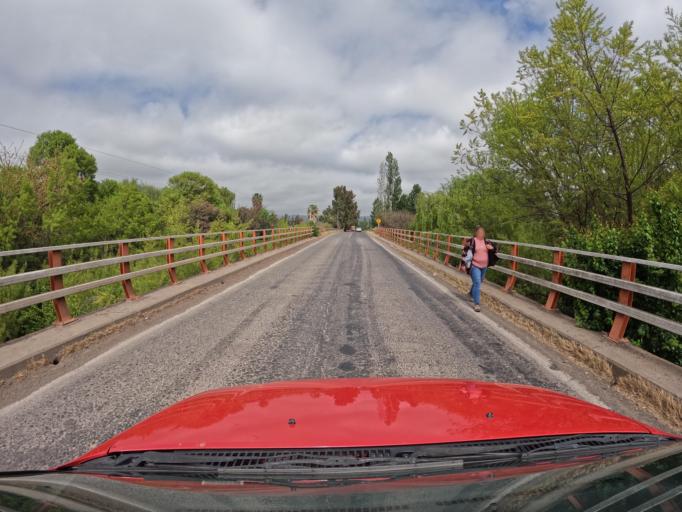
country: CL
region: O'Higgins
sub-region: Provincia de Colchagua
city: Santa Cruz
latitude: -34.6763
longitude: -71.3548
